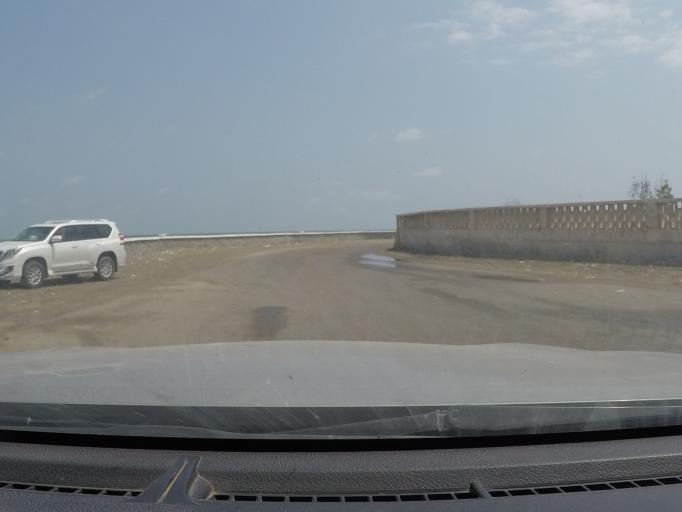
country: YE
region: Aden
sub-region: Khur Maksar
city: Khawr Maksar
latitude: 12.8142
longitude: 45.0428
